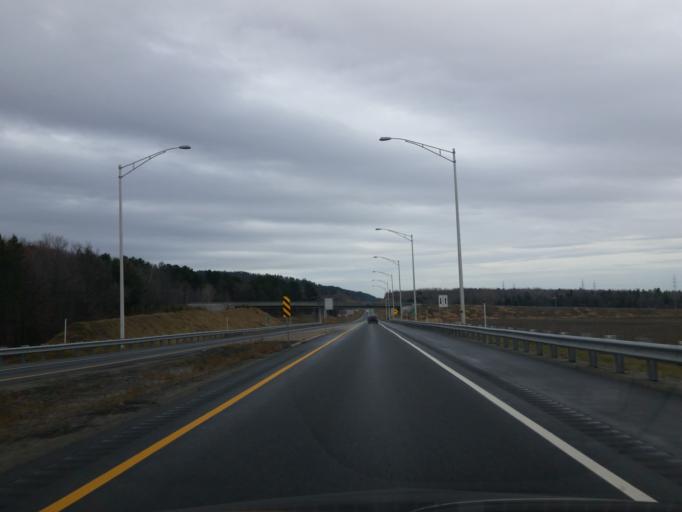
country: CA
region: Quebec
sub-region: Outaouais
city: Papineauville
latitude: 45.6716
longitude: -74.9205
